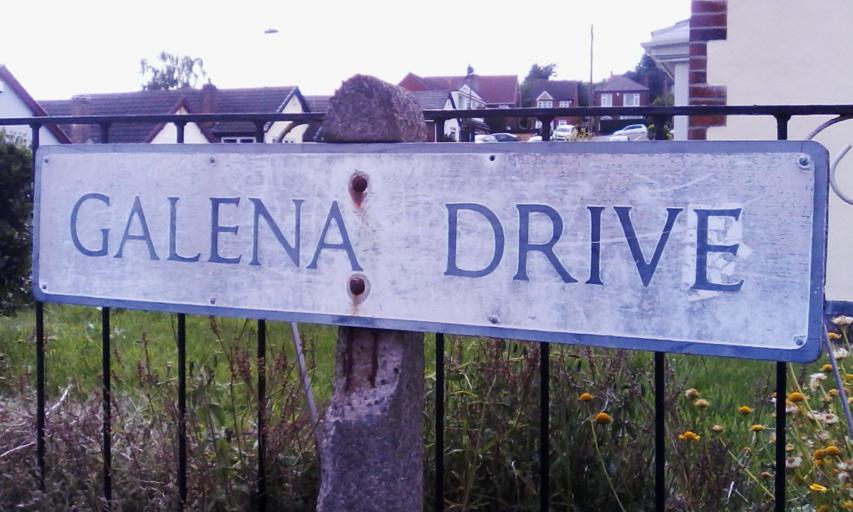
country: GB
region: England
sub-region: Nottingham
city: Nottingham
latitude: 52.9663
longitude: -1.1191
